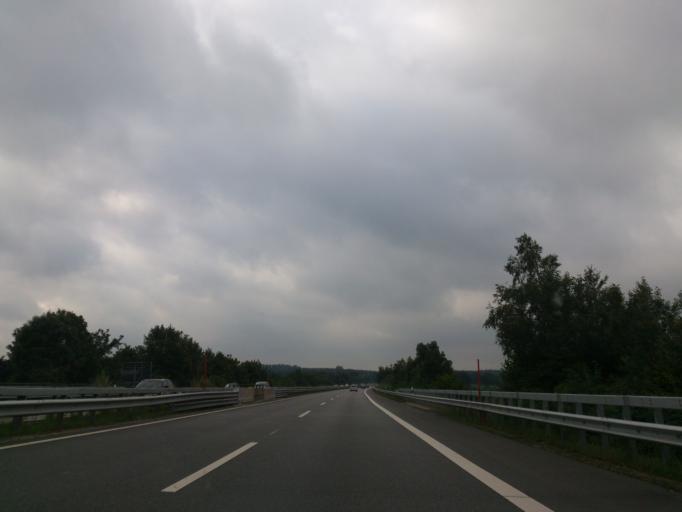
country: DE
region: Schleswig-Holstein
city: Kaaks
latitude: 53.9968
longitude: 9.4853
